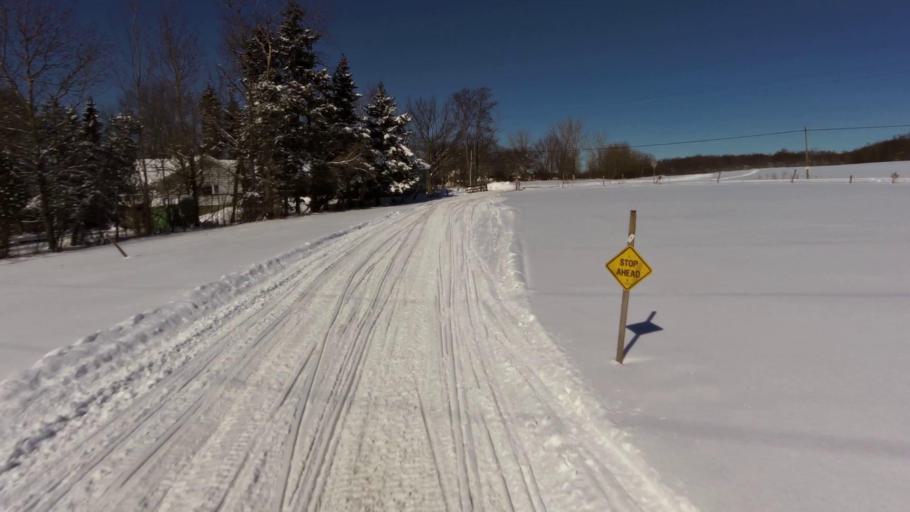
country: US
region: New York
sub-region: Chautauqua County
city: Mayville
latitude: 42.2614
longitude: -79.4507
